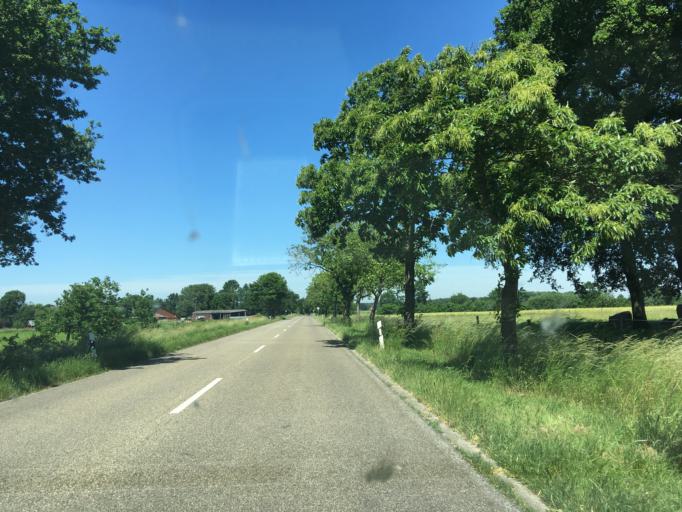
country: DE
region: North Rhine-Westphalia
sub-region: Regierungsbezirk Munster
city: Raesfeld
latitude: 51.7865
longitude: 6.8188
